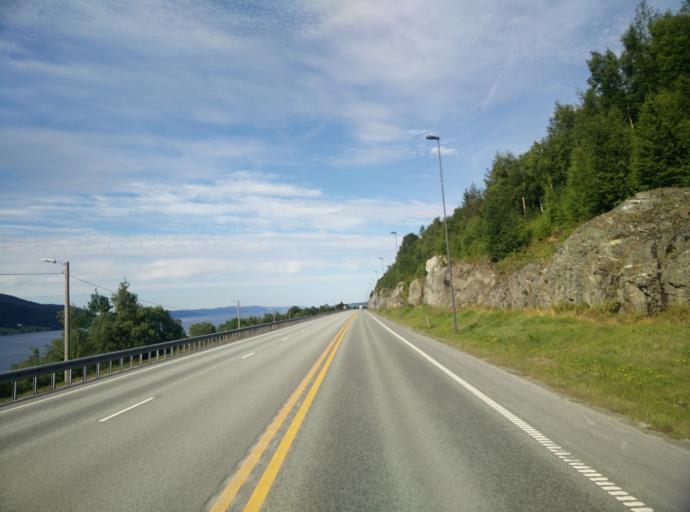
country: NO
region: Sor-Trondelag
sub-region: Orkdal
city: Orkanger
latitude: 63.3214
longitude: 9.8869
